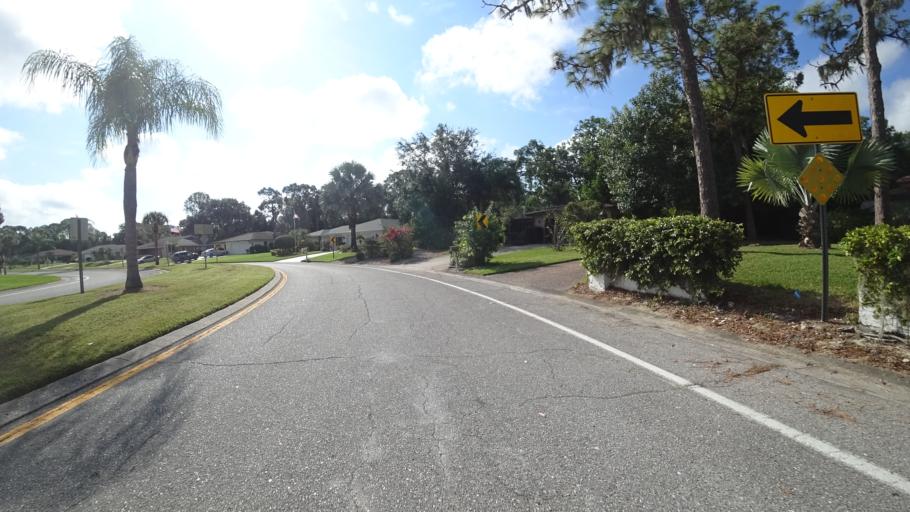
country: US
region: Florida
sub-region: Sarasota County
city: Desoto Lakes
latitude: 27.4006
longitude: -82.5009
